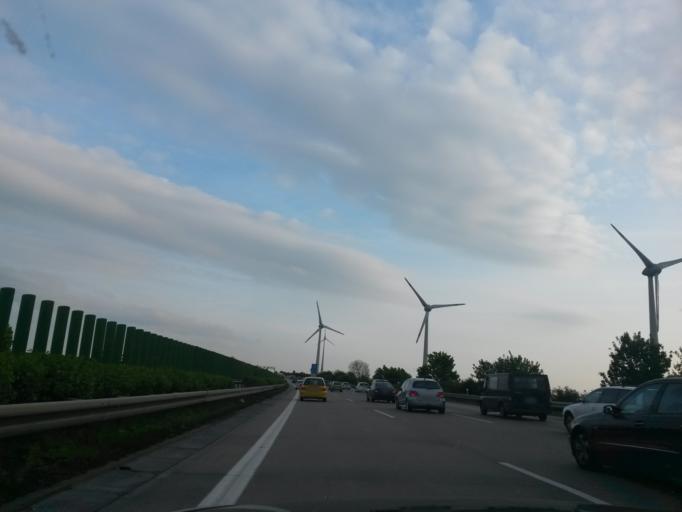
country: DE
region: Saxony-Anhalt
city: Stossen
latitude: 51.1243
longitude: 11.9585
